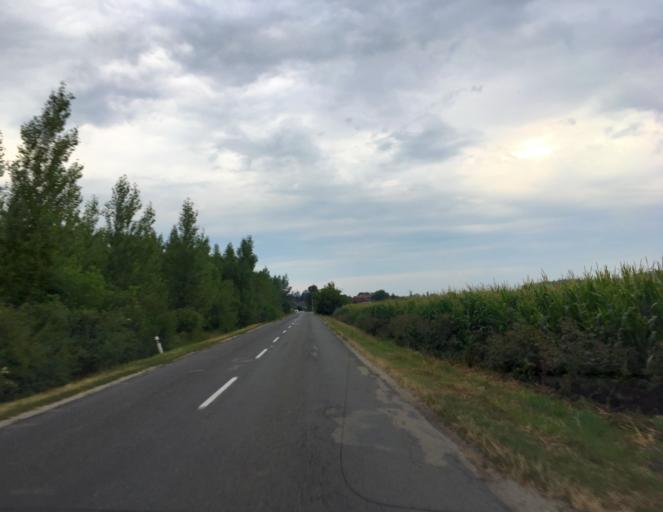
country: SK
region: Trnavsky
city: Gabcikovo
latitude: 47.8829
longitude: 17.6574
